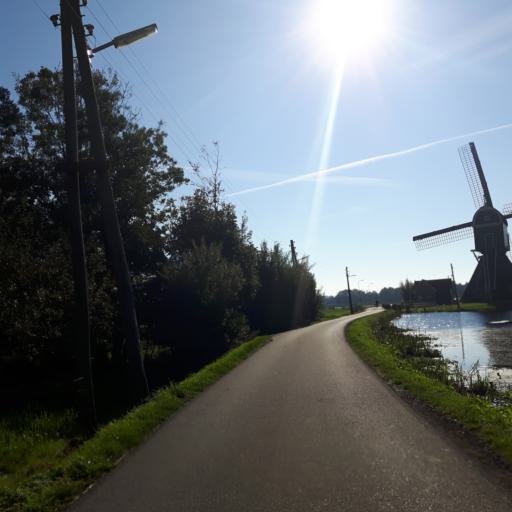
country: NL
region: South Holland
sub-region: Gemeente Schoonhoven
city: Schoonhoven
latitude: 51.9606
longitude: 4.8461
